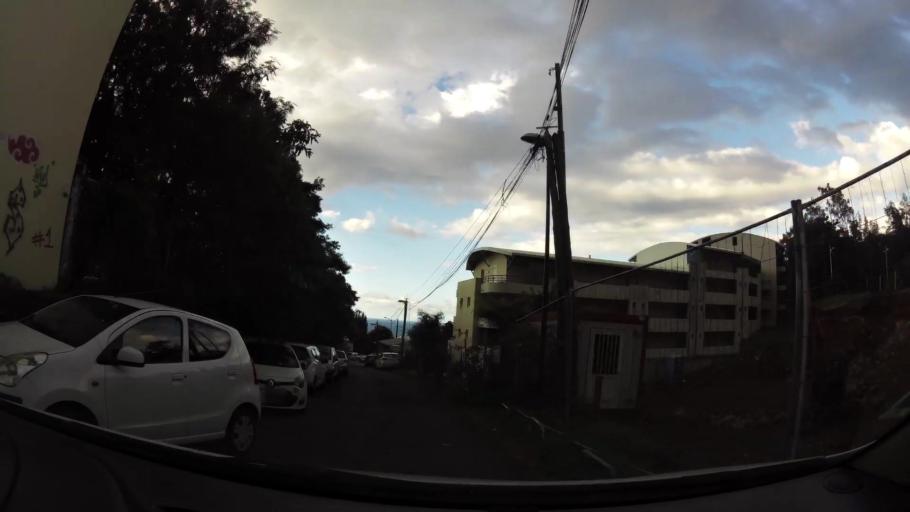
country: RE
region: Reunion
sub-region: Reunion
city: Saint-Denis
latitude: -20.8941
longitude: 55.4425
